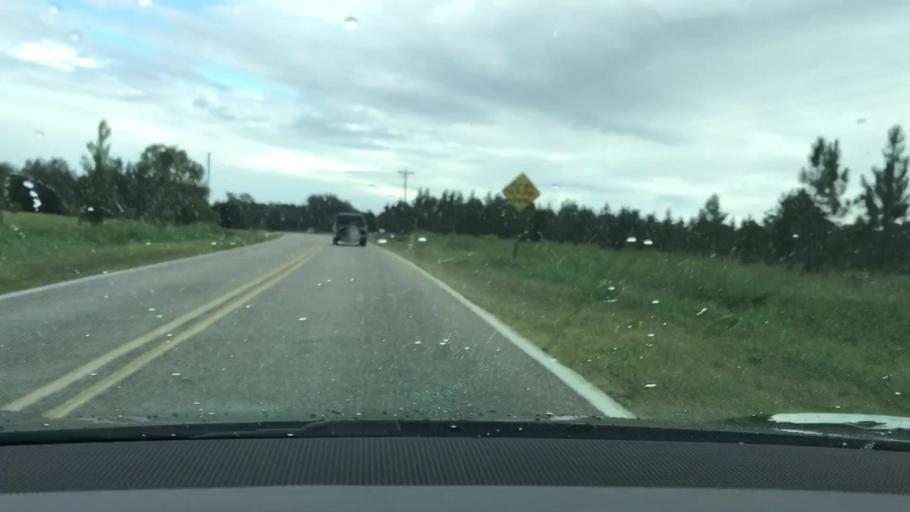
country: US
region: Alabama
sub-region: Geneva County
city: Samson
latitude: 31.1316
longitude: -86.1332
